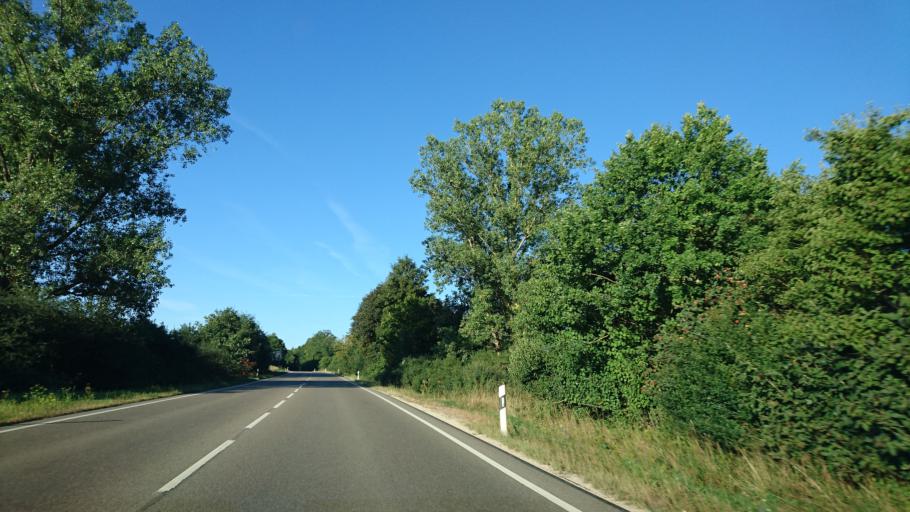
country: DE
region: Bavaria
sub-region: Regierungsbezirk Mittelfranken
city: Langenaltheim
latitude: 48.8964
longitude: 10.8801
